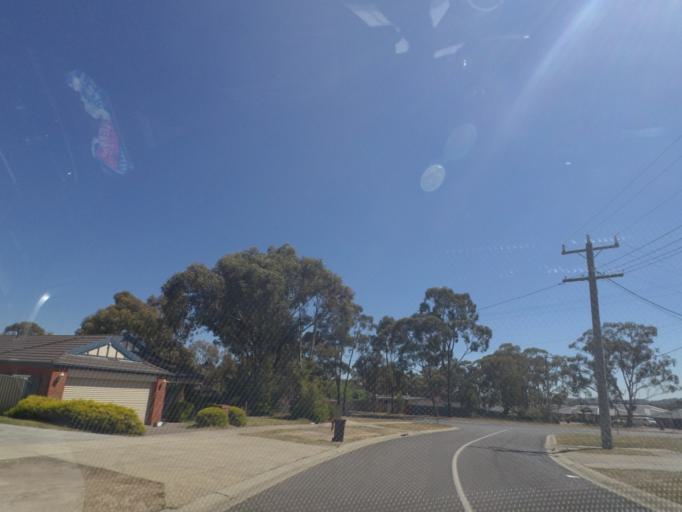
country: AU
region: Victoria
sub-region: Whittlesea
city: Whittlesea
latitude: -37.2070
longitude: 145.0622
